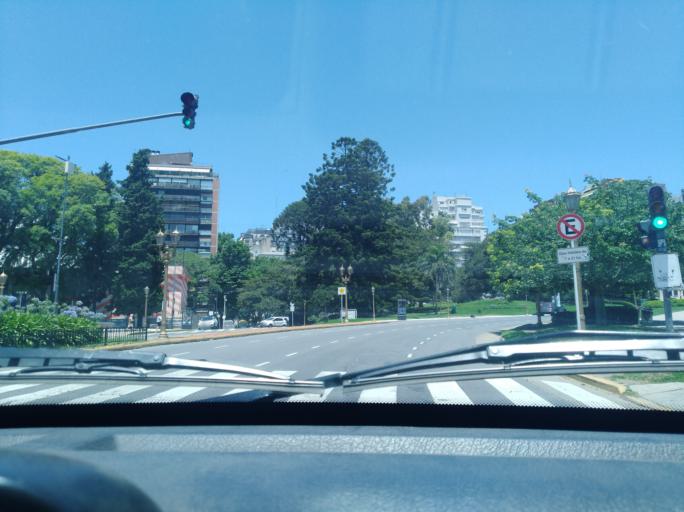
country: AR
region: Buenos Aires F.D.
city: Retiro
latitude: -34.5853
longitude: -58.3906
